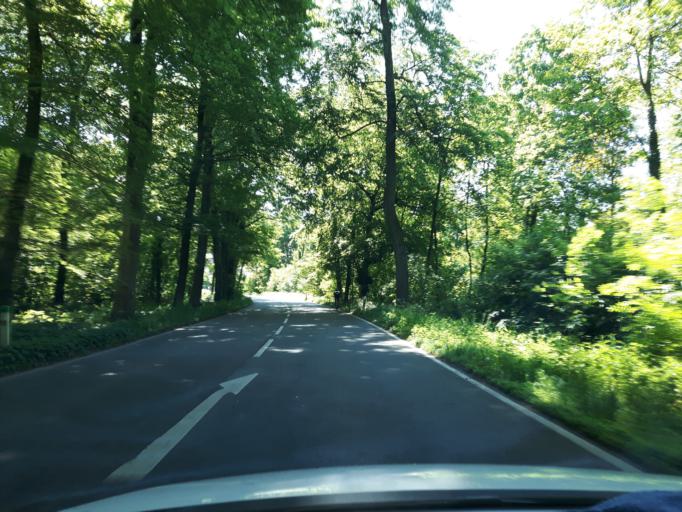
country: DE
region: North Rhine-Westphalia
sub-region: Regierungsbezirk Dusseldorf
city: Ratingen
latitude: 51.3348
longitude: 6.7978
